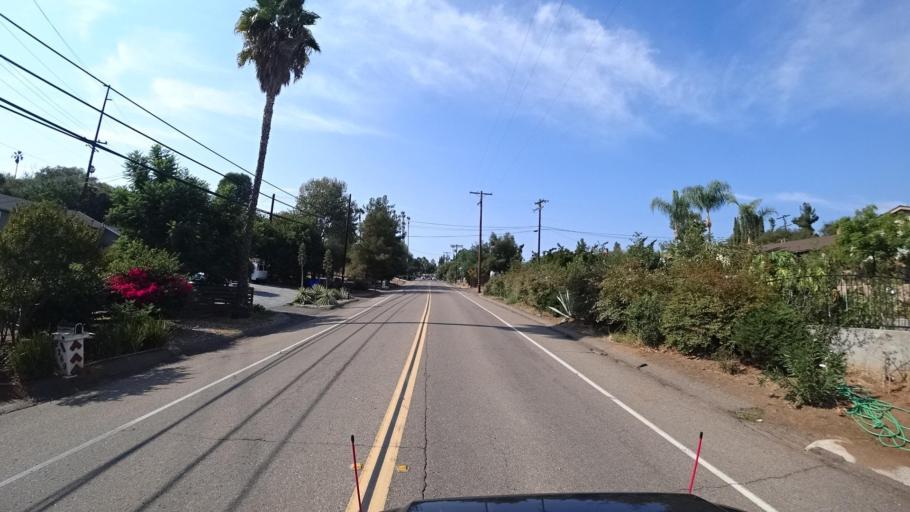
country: US
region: California
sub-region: San Diego County
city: Escondido
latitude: 33.0964
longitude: -117.0634
